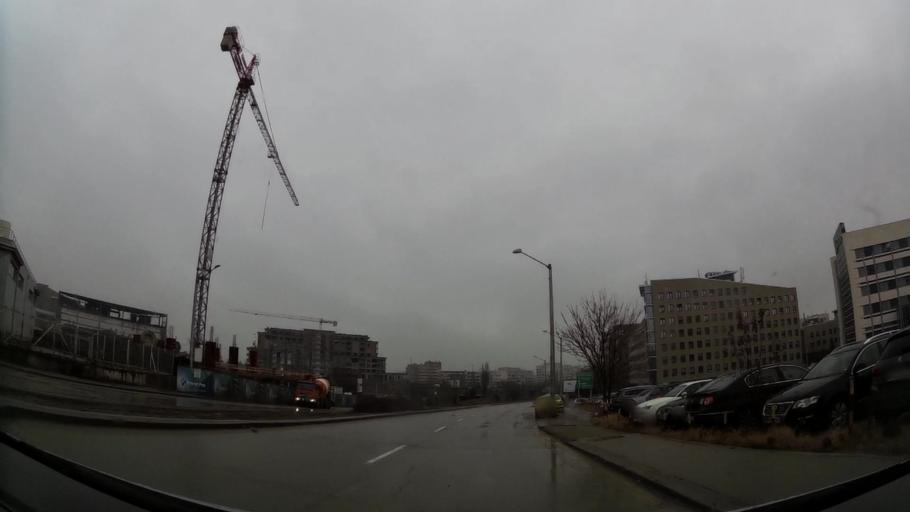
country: BG
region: Sofia-Capital
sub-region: Stolichna Obshtina
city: Sofia
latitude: 42.6245
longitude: 23.3746
